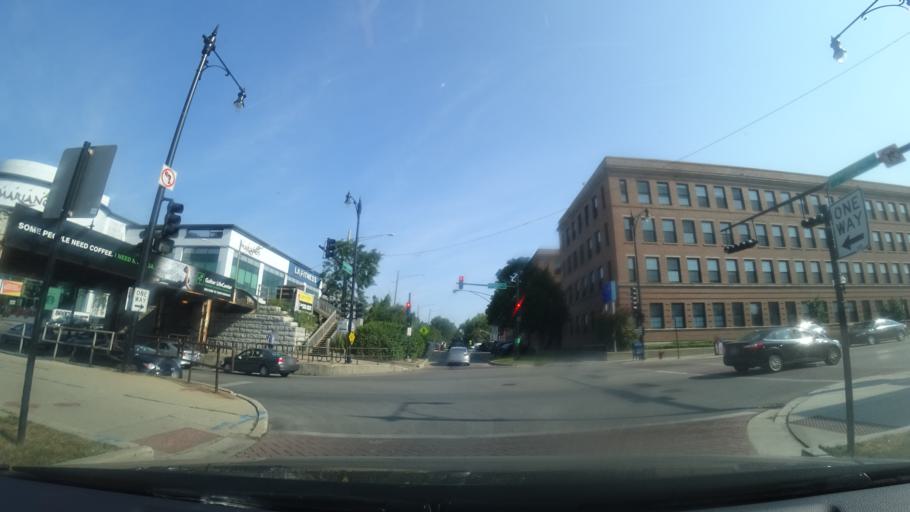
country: US
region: Illinois
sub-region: Cook County
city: Lincolnwood
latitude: 41.9687
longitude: -87.6741
